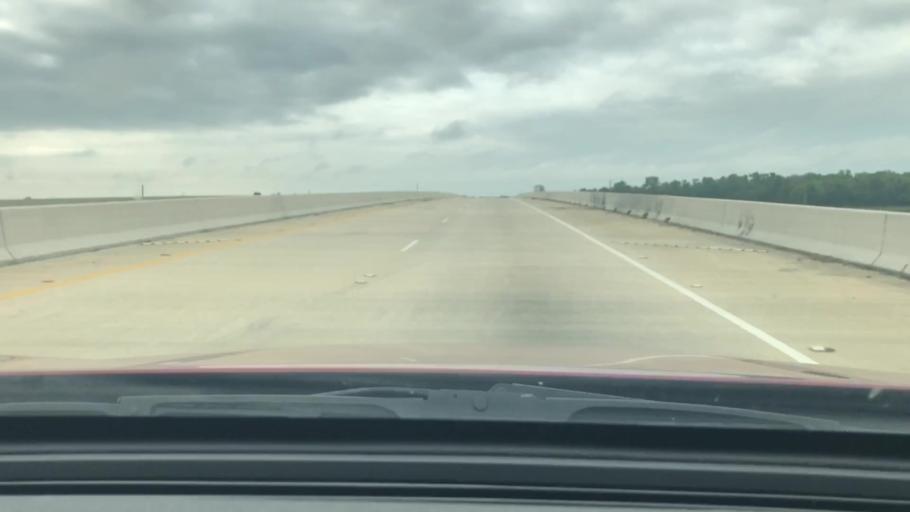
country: US
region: Louisiana
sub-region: Caddo Parish
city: Blanchard
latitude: 32.6762
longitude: -93.8510
